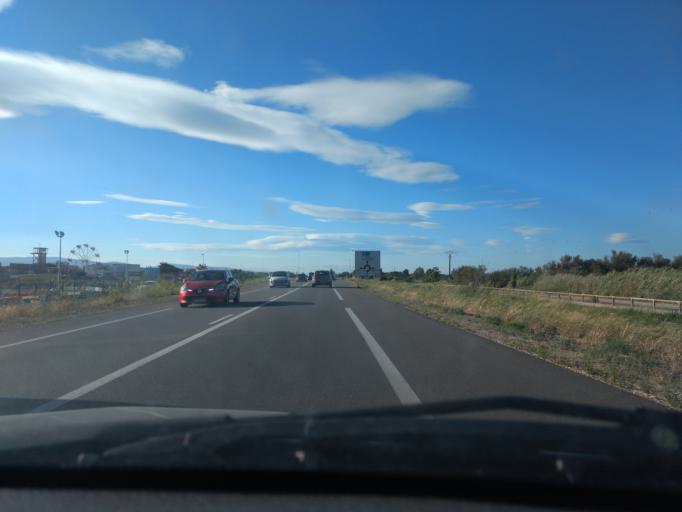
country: FR
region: Languedoc-Roussillon
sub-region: Departement des Pyrenees-Orientales
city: Torreilles
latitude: 42.7589
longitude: 3.0200
